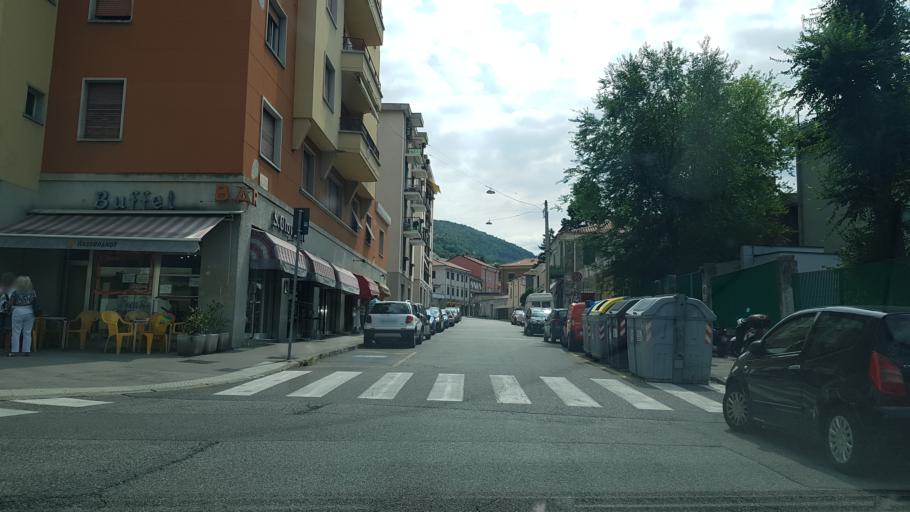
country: IT
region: Friuli Venezia Giulia
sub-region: Provincia di Trieste
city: Trieste
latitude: 45.6562
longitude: 13.8054
